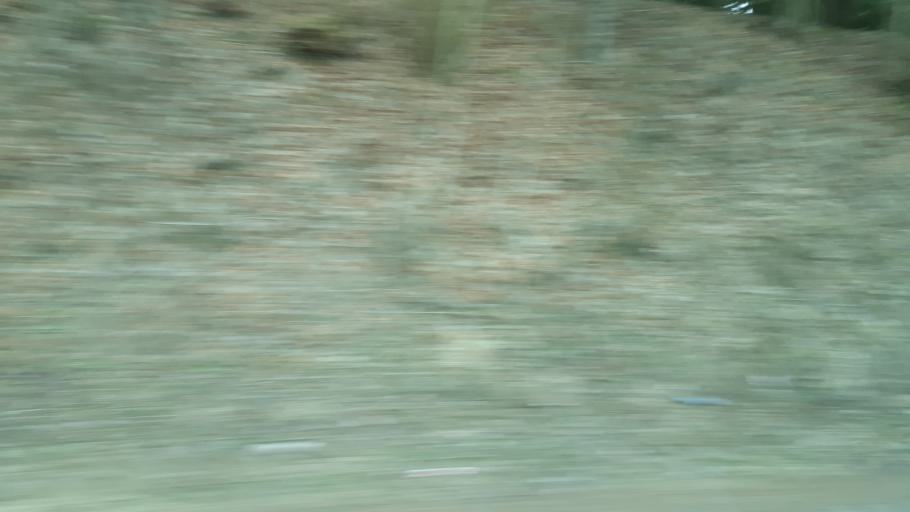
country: PL
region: Podlasie
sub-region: Suwalki
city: Suwalki
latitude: 54.2808
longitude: 22.9468
